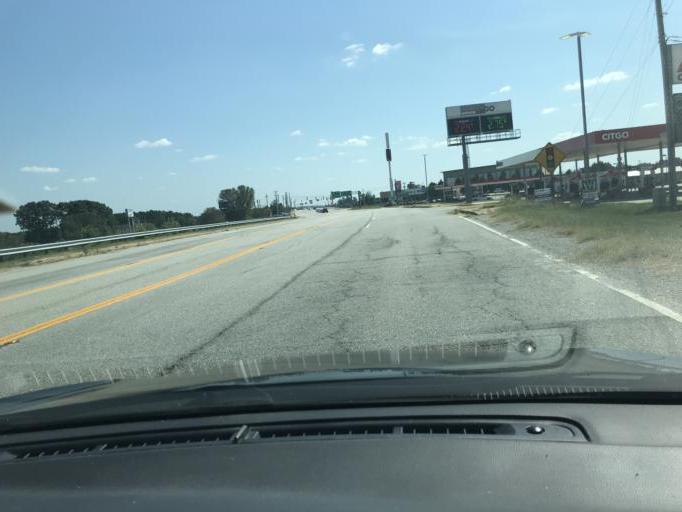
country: US
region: South Carolina
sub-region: Cherokee County
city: Gaffney
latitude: 35.0861
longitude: -81.7087
